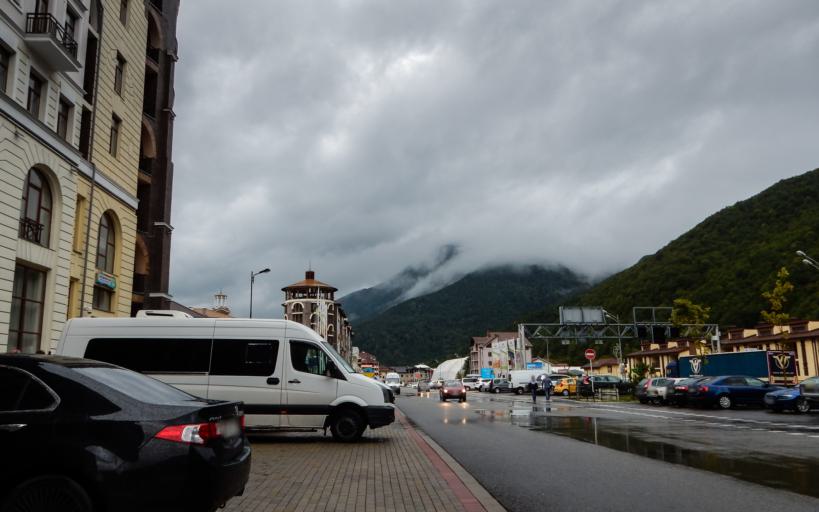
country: RU
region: Krasnodarskiy
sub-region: Sochi City
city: Krasnaya Polyana
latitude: 43.6831
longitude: 40.2686
